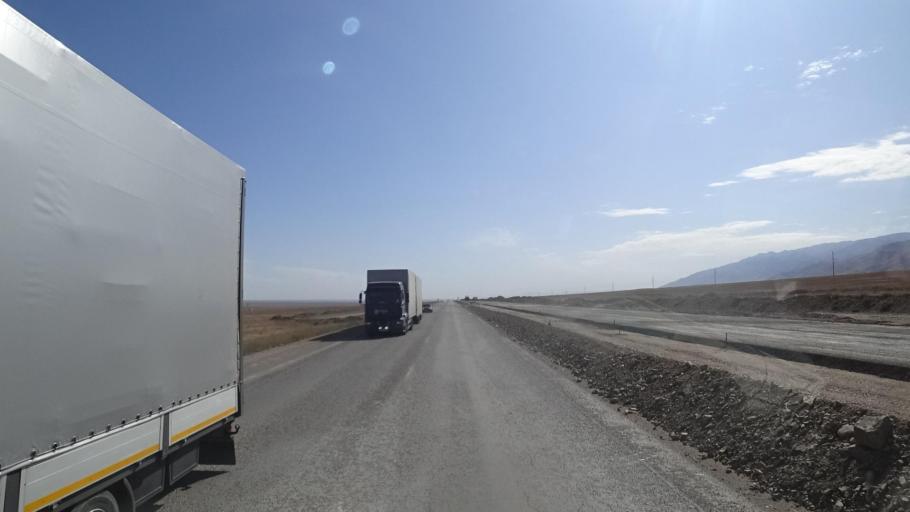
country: KG
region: Chuy
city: Ivanovka
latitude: 43.3832
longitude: 75.1843
